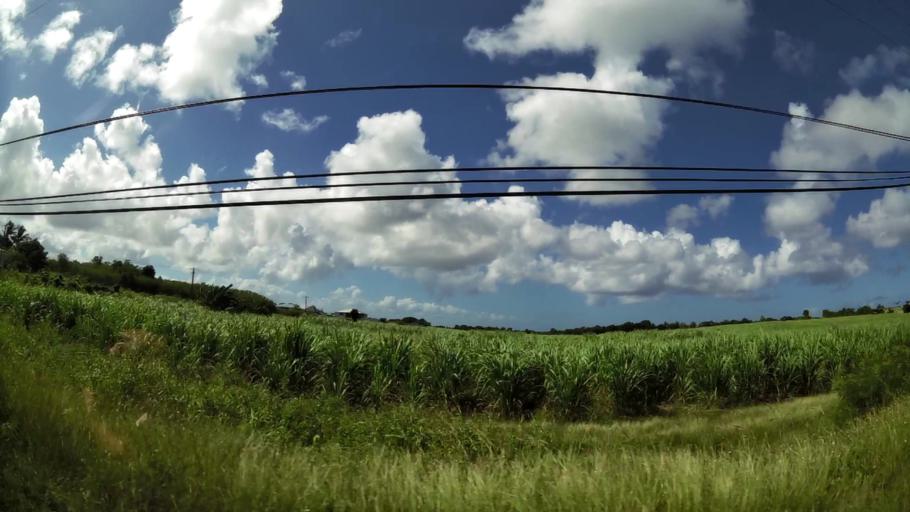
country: GP
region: Guadeloupe
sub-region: Guadeloupe
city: Anse-Bertrand
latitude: 16.4602
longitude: -61.4820
